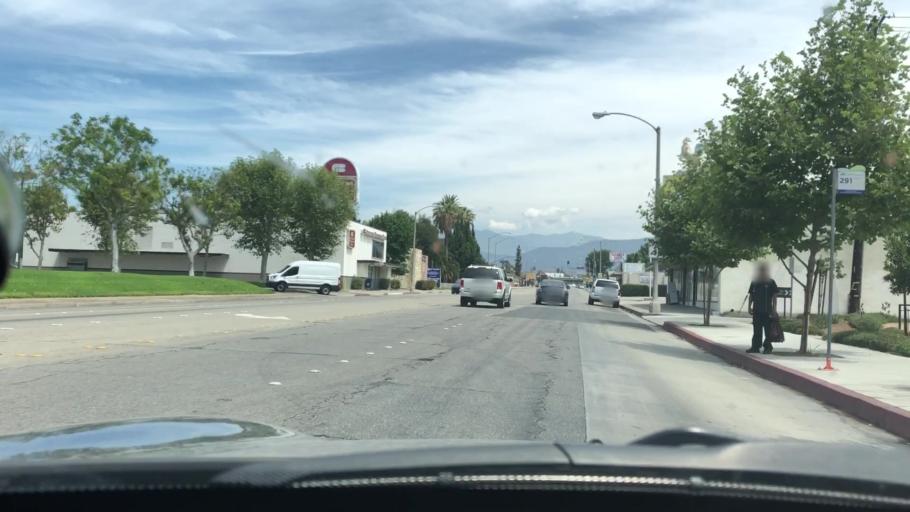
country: US
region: California
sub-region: Los Angeles County
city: Pomona
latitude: 34.0680
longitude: -117.7520
